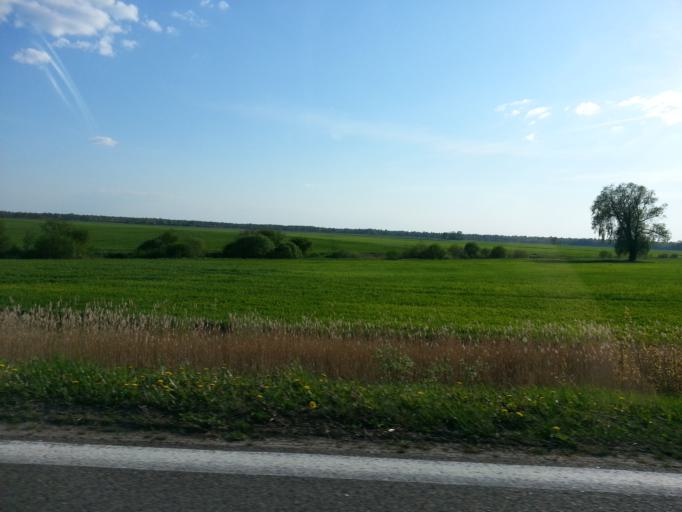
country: LT
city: Ramygala
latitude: 55.5380
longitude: 24.5401
